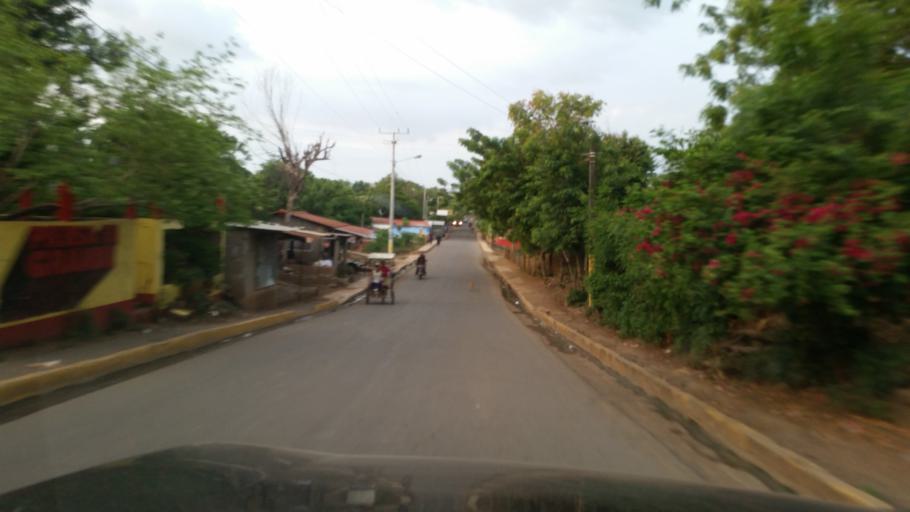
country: NI
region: Managua
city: Masachapa
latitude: 11.7818
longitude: -86.5149
